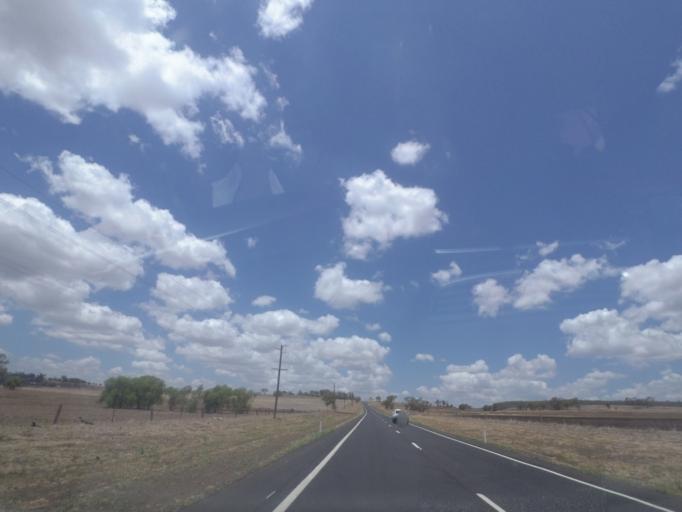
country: AU
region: Queensland
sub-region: Toowoomba
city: Top Camp
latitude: -27.7229
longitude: 151.9117
